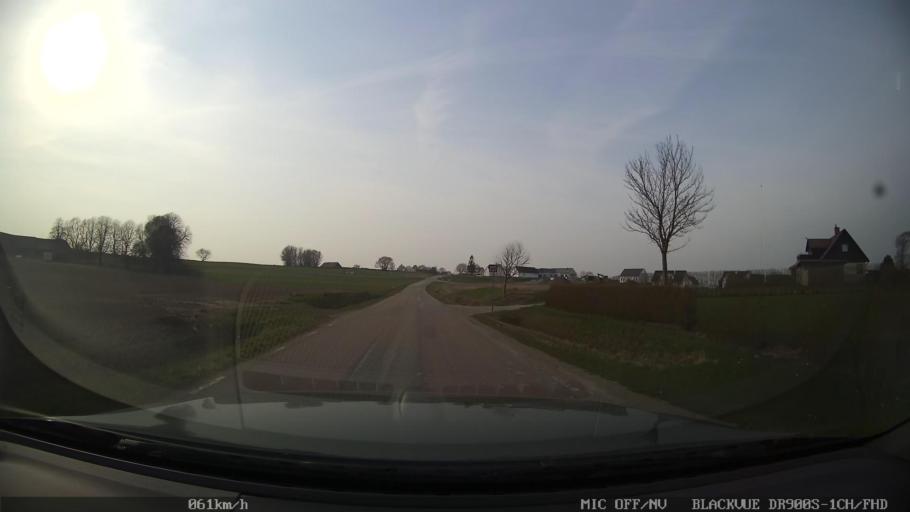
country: SE
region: Skane
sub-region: Ystads Kommun
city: Ystad
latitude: 55.4680
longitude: 13.8097
